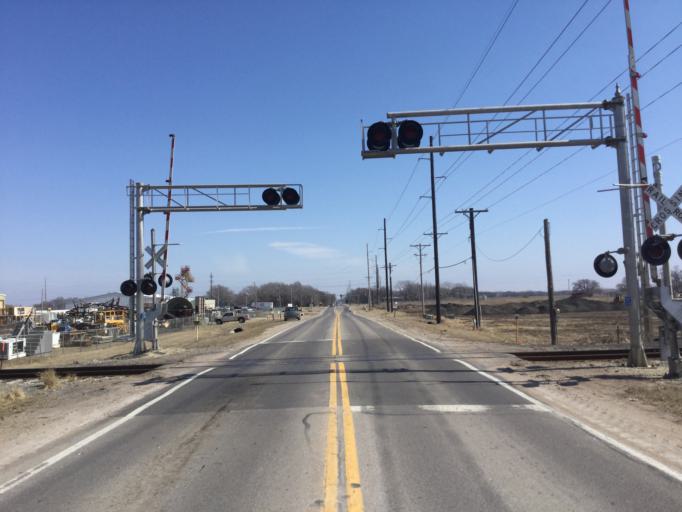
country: US
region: Kansas
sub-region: Sedgwick County
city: Haysville
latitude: 37.6224
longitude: -97.3930
